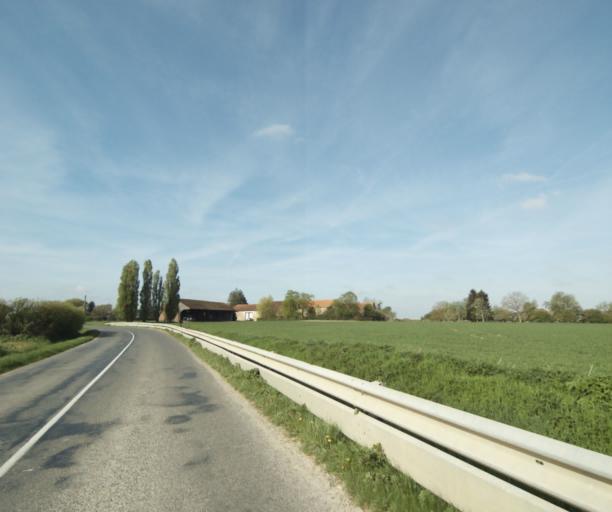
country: FR
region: Ile-de-France
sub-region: Departement de Seine-et-Marne
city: Nangis
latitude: 48.5779
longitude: 3.0416
